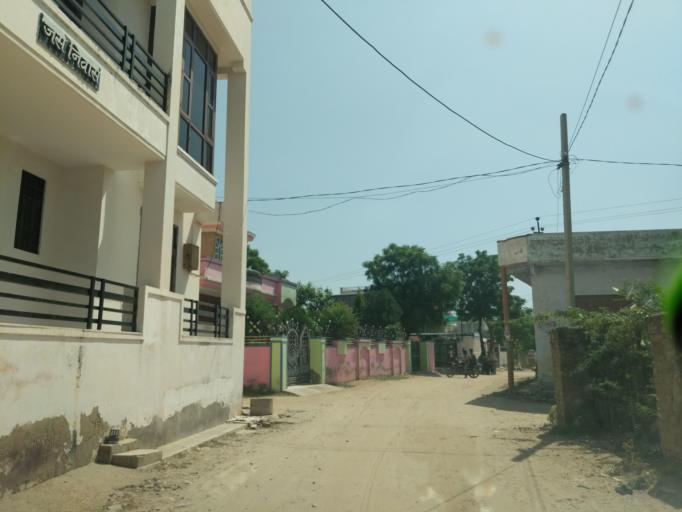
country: IN
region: Rajasthan
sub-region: Nagaur
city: Makrana
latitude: 27.0269
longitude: 74.7527
